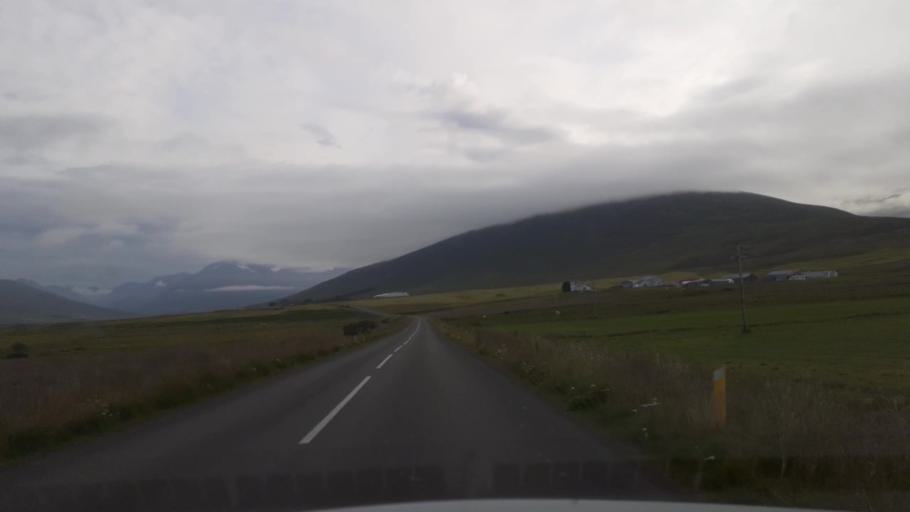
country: IS
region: Northeast
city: Dalvik
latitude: 65.9614
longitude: -18.5420
